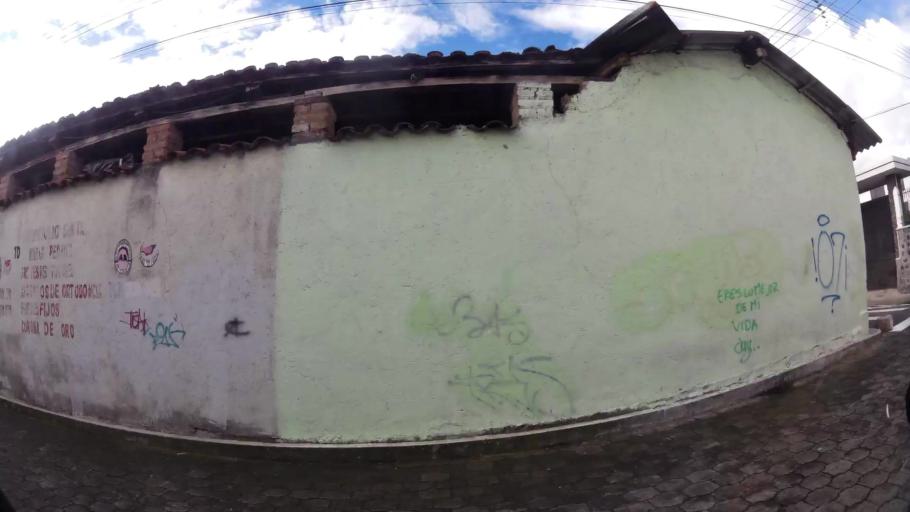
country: EC
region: Pichincha
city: Sangolqui
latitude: -0.3331
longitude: -78.4456
